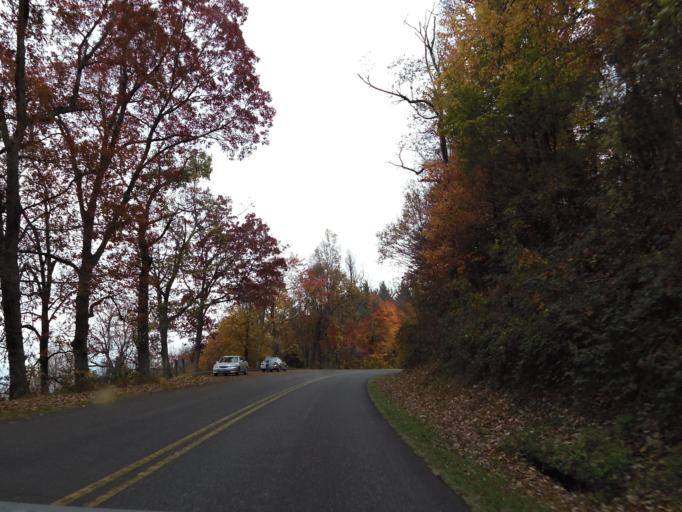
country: US
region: North Carolina
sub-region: Ashe County
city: West Jefferson
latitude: 36.2822
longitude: -81.4129
